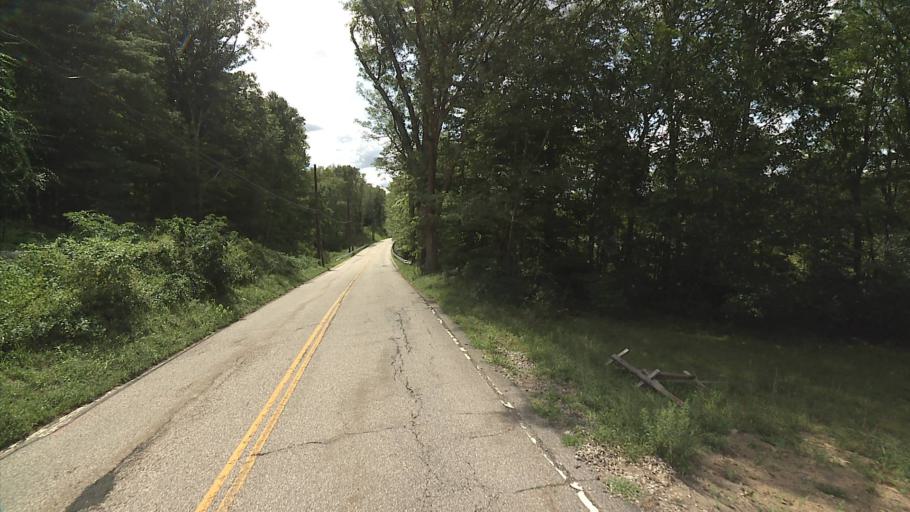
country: US
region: Connecticut
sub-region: New London County
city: Lisbon
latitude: 41.6079
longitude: -72.0371
